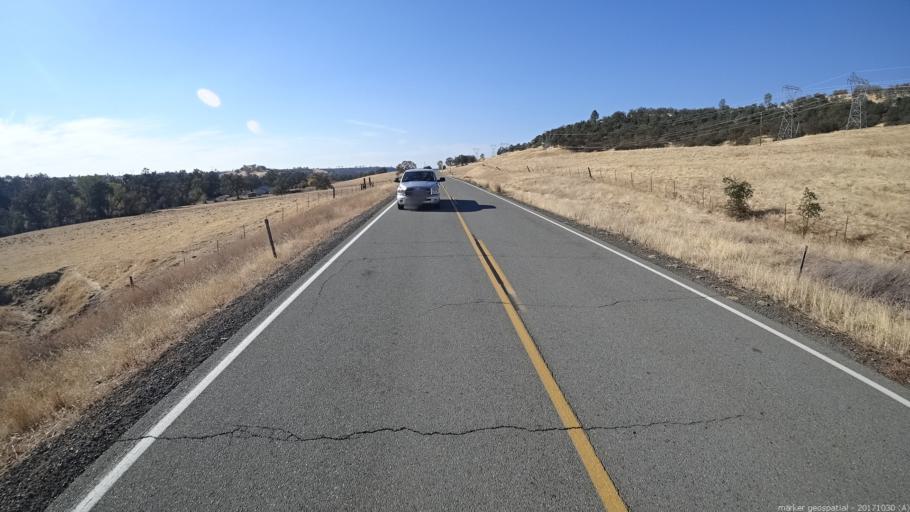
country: US
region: California
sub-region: Shasta County
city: Bella Vista
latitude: 40.6492
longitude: -122.0770
